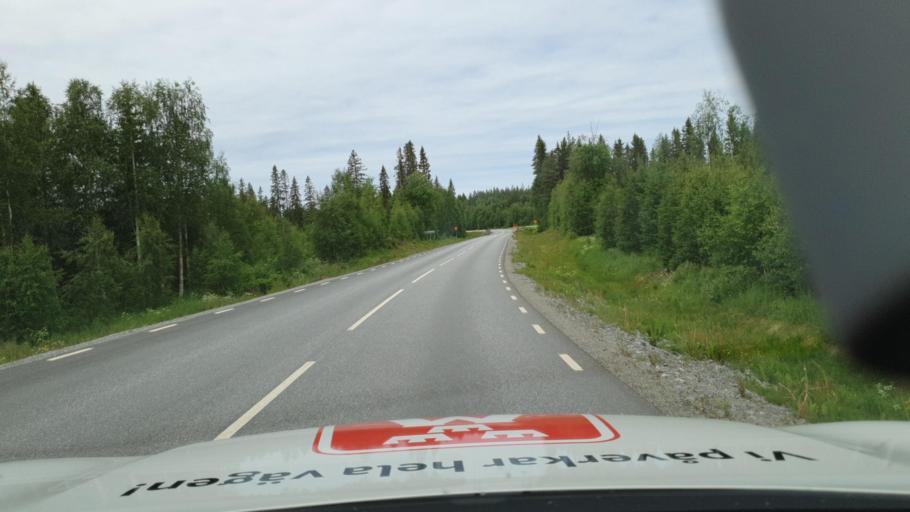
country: SE
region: Vaesterbotten
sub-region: Skelleftea Kommun
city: Langsele
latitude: 64.5310
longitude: 20.3213
